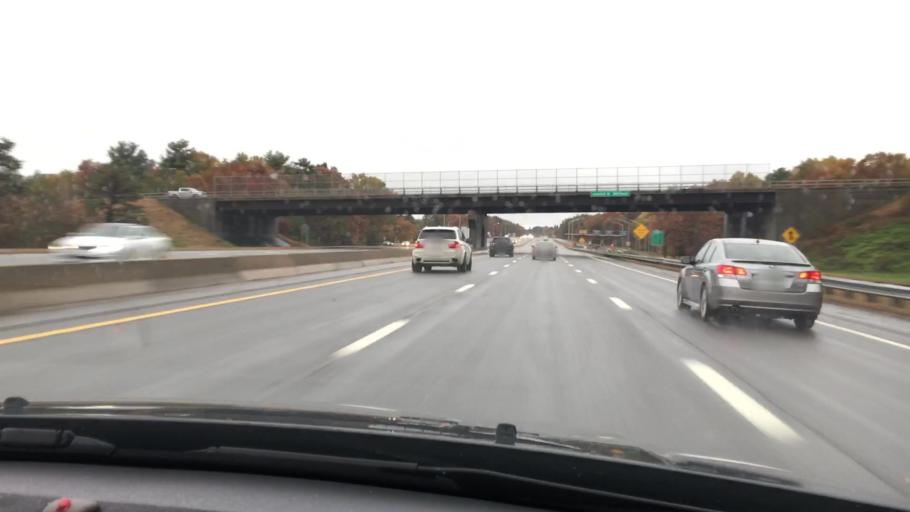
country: US
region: New Hampshire
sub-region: Hillsborough County
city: Litchfield
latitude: 42.8221
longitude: -71.4958
